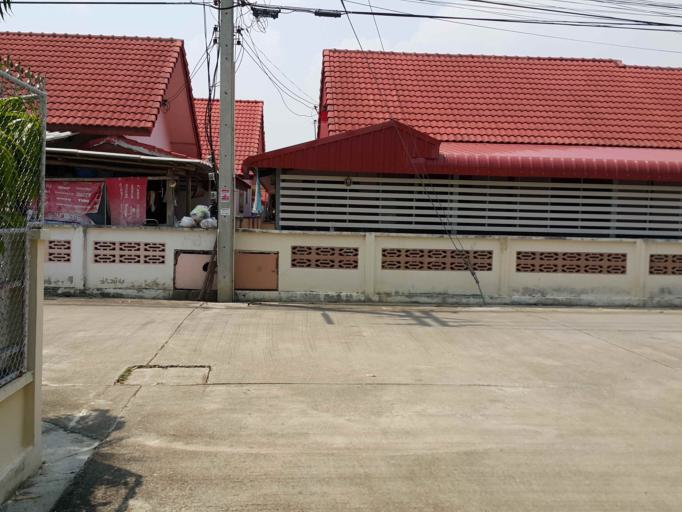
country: TH
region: Chiang Mai
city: San Kamphaeng
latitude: 18.7909
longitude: 99.0913
